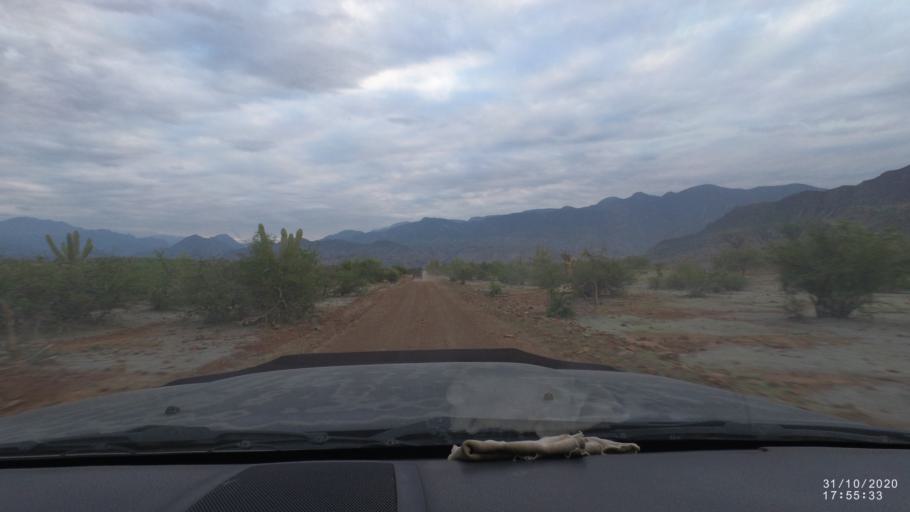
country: BO
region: Chuquisaca
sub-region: Provincia Zudanez
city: Mojocoya
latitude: -18.6448
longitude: -64.5281
